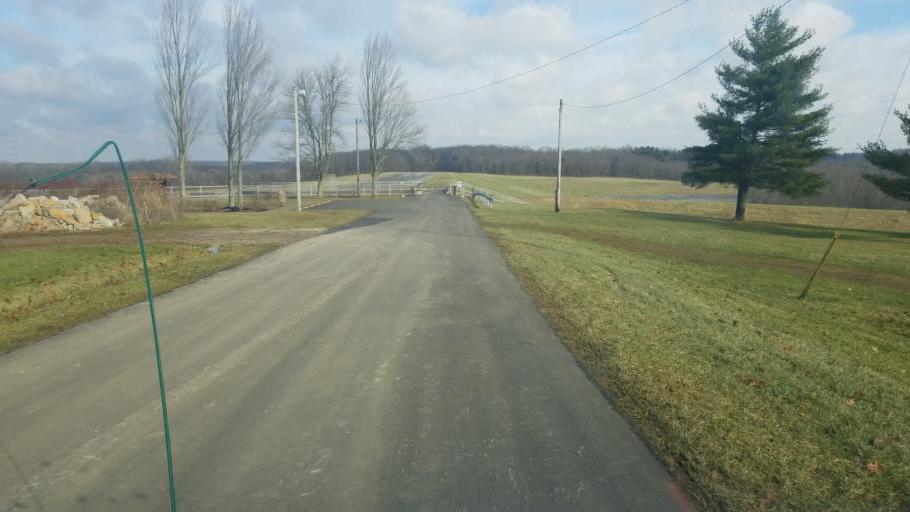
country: US
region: Ohio
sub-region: Knox County
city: Fredericktown
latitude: 40.5029
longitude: -82.5778
